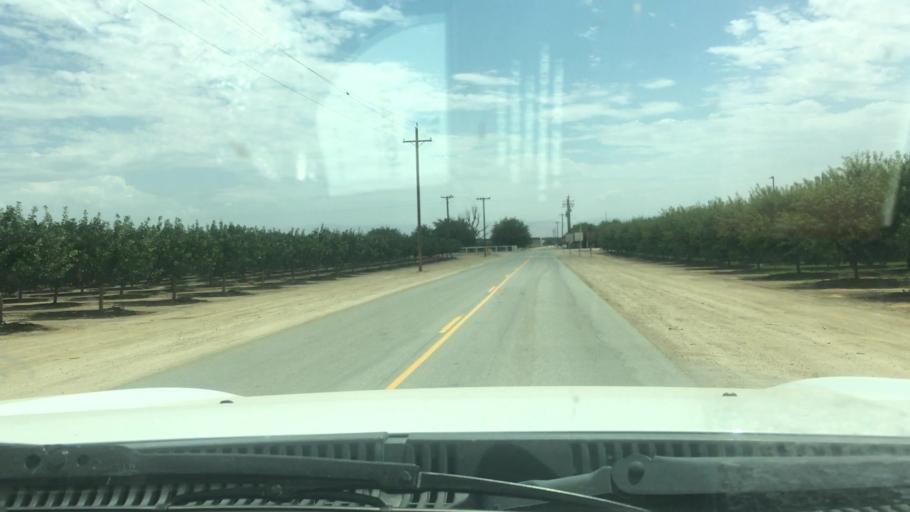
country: US
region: California
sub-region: Kern County
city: Shafter
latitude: 35.5587
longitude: -119.1532
